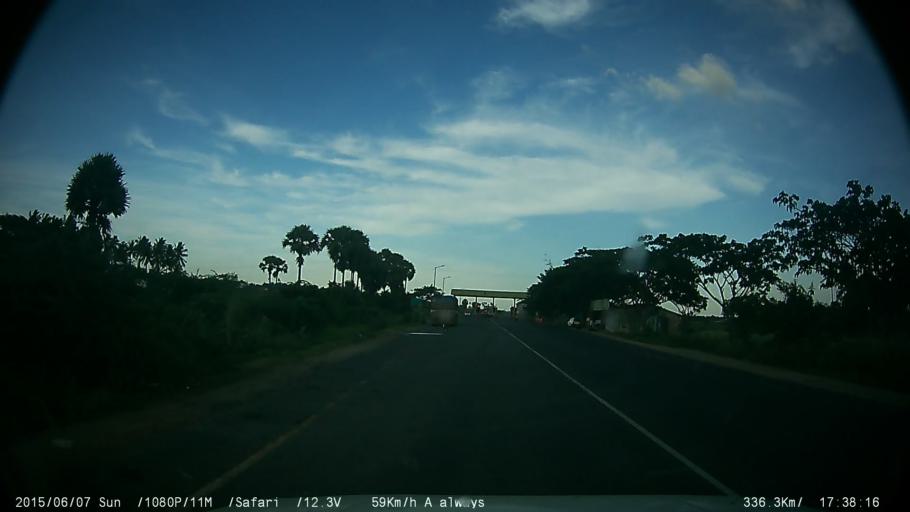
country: IN
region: Tamil Nadu
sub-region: Coimbatore
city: Madukkarai
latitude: 10.8954
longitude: 76.9439
